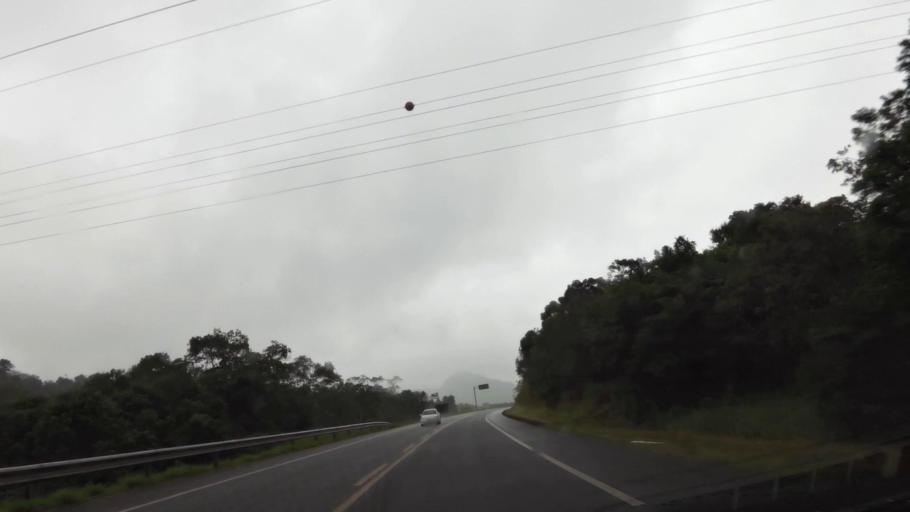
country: BR
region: Espirito Santo
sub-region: Guarapari
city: Guarapari
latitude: -20.6353
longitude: -40.5264
